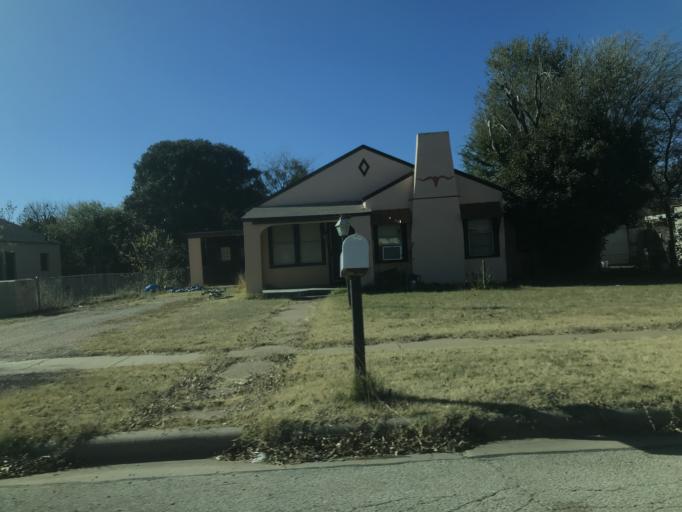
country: US
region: Texas
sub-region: Taylor County
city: Abilene
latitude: 32.4364
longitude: -99.7571
